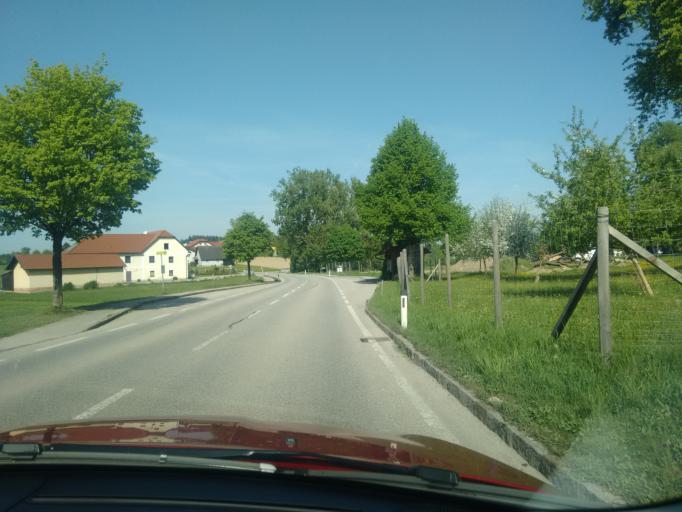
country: AT
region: Upper Austria
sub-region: Politischer Bezirk Grieskirchen
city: Bad Schallerbach
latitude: 48.3023
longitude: 13.9243
